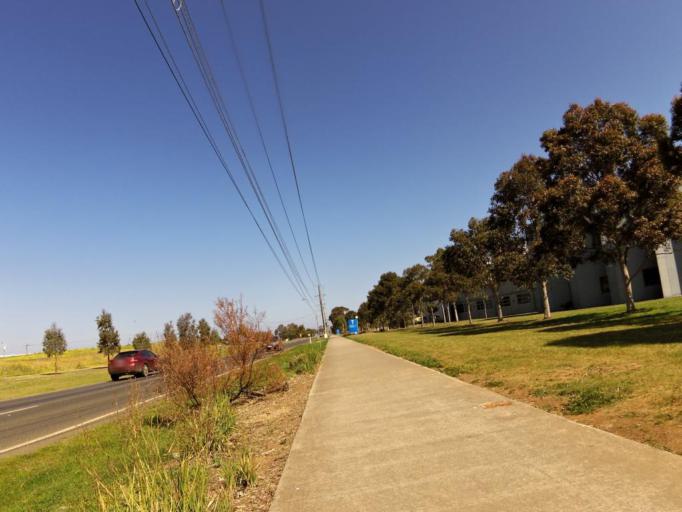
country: AU
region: Victoria
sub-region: Wyndham
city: Hoppers Crossing
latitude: -37.8888
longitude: 144.7005
